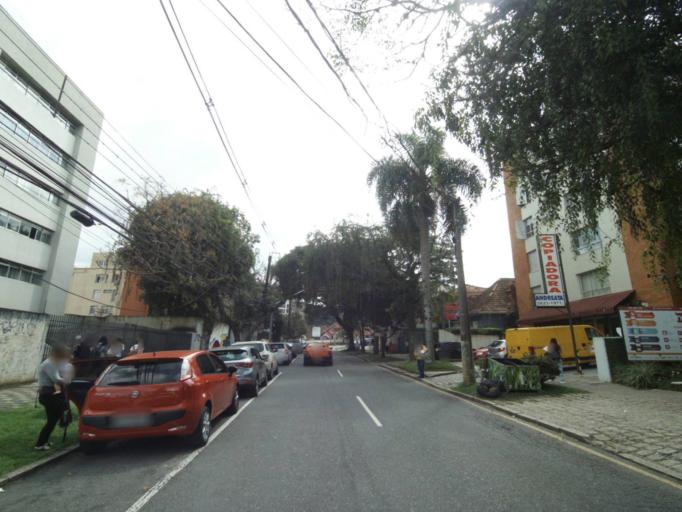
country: BR
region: Parana
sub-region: Curitiba
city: Curitiba
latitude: -25.4245
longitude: -49.2637
